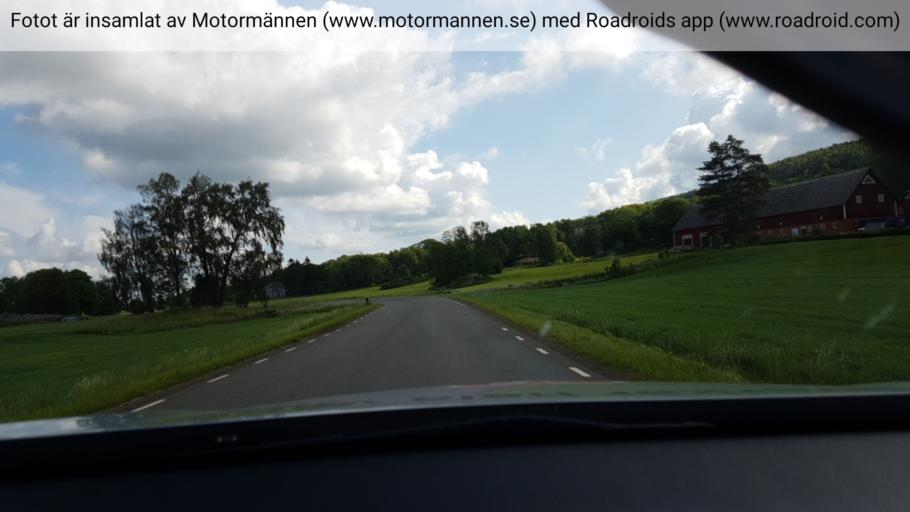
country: SE
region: Vaestra Goetaland
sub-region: Skara Kommun
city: Axvall
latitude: 58.3549
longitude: 13.6208
